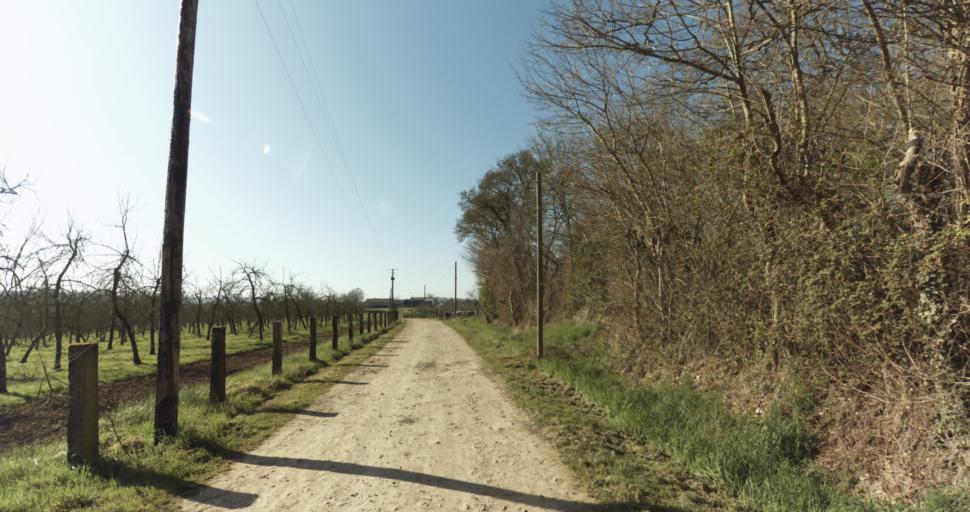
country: FR
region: Lower Normandy
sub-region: Departement du Calvados
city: Saint-Pierre-sur-Dives
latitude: 48.9856
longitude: 0.0004
